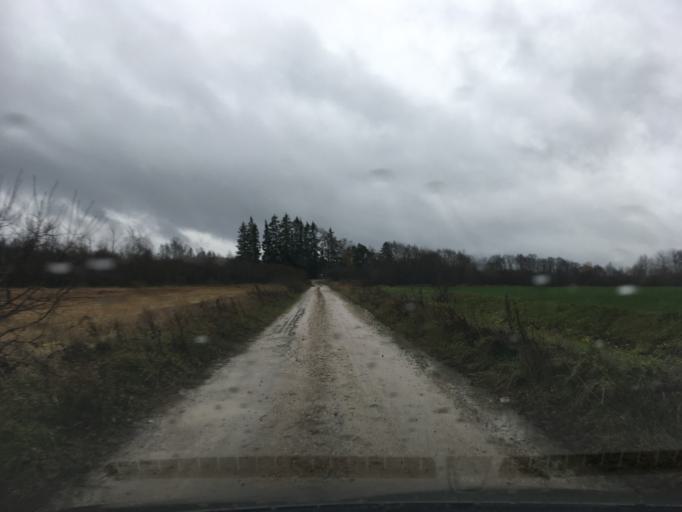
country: EE
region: Laeaene
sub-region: Lihula vald
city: Lihula
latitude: 58.7018
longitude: 23.8558
